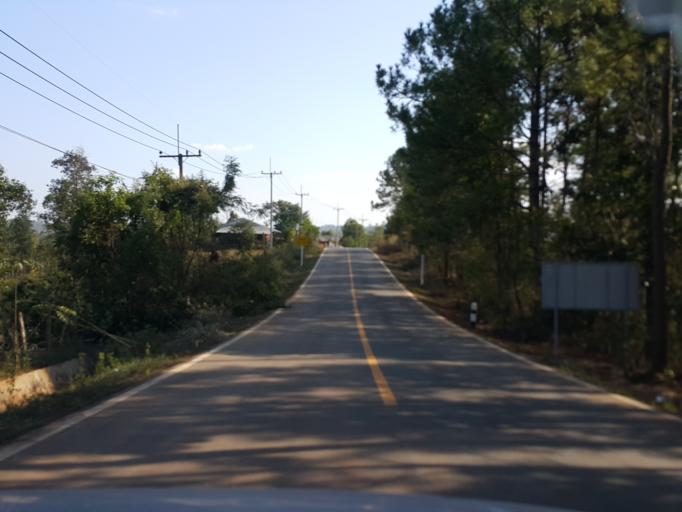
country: TH
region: Chiang Mai
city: Mae Wang
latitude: 18.6922
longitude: 98.5656
